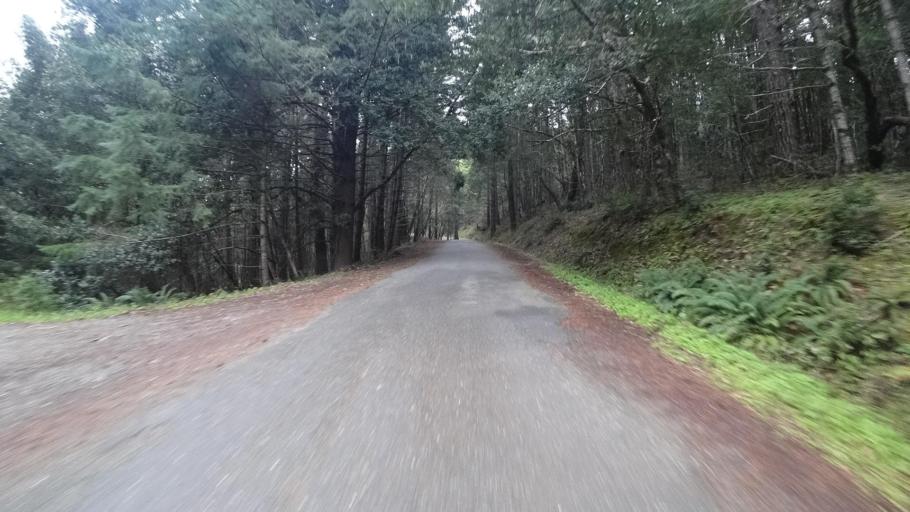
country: US
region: California
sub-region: Humboldt County
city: Redway
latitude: 40.2145
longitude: -123.7476
